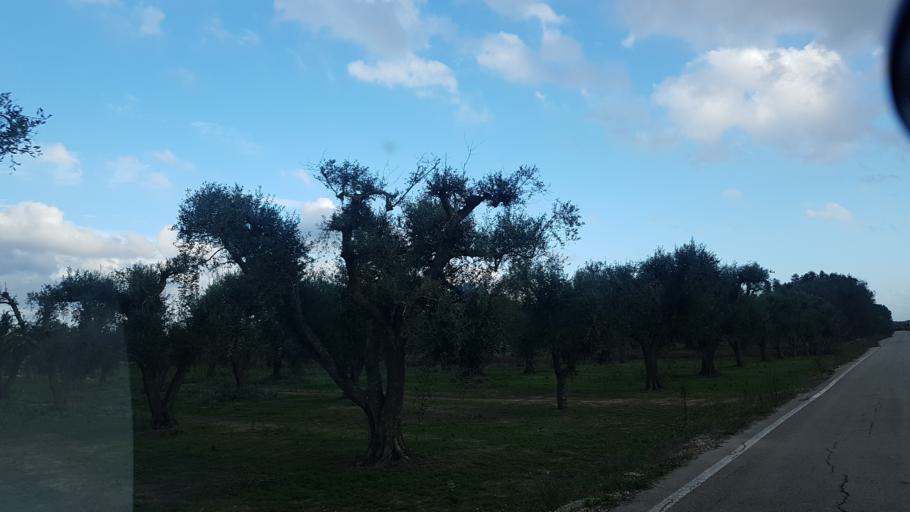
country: IT
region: Apulia
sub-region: Provincia di Brindisi
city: San Pietro Vernotico
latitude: 40.5117
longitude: 18.0189
